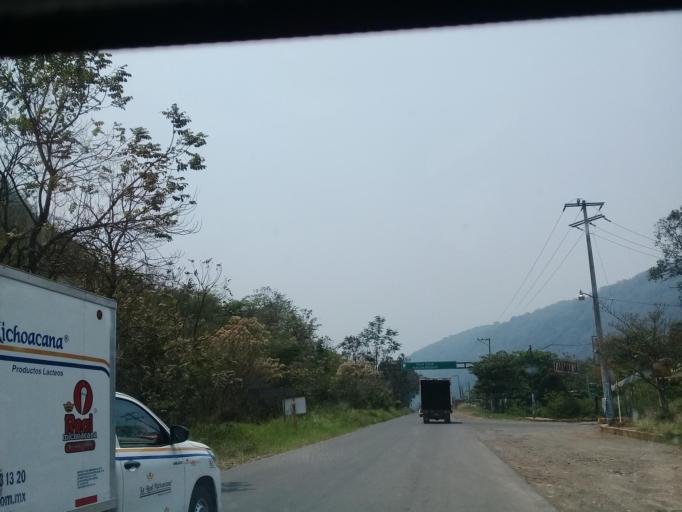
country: MX
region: Veracruz
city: Tezonapa
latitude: 18.6112
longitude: -96.6936
